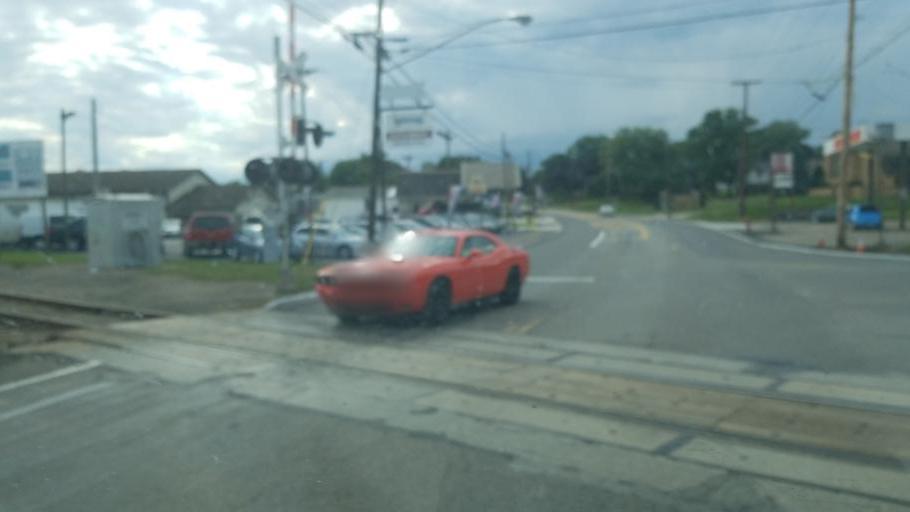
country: US
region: Ohio
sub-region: Tuscarawas County
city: Sugarcreek
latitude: 40.5085
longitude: -81.6313
